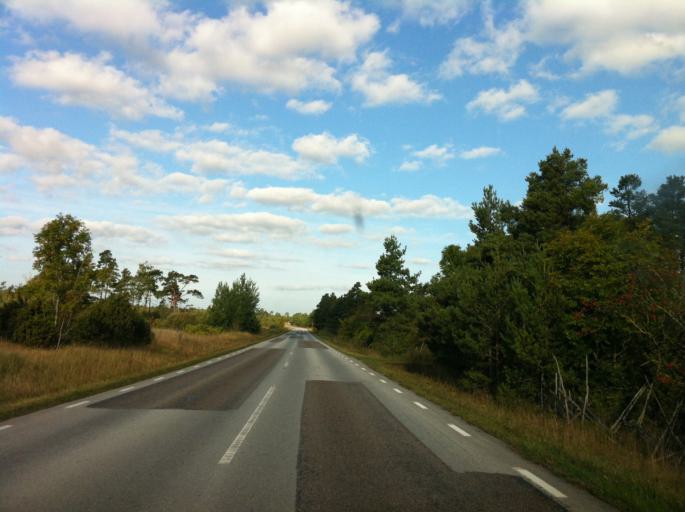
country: SE
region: Gotland
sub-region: Gotland
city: Slite
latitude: 57.4365
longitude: 18.7529
